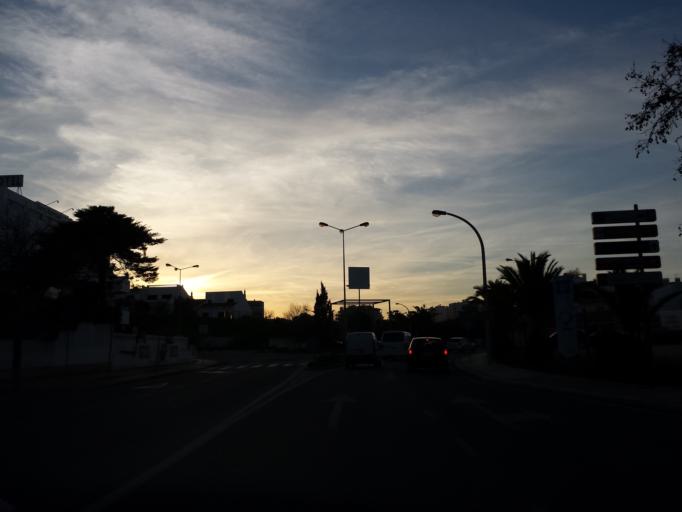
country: PT
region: Faro
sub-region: Lagos
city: Lagos
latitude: 37.0954
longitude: -8.6740
